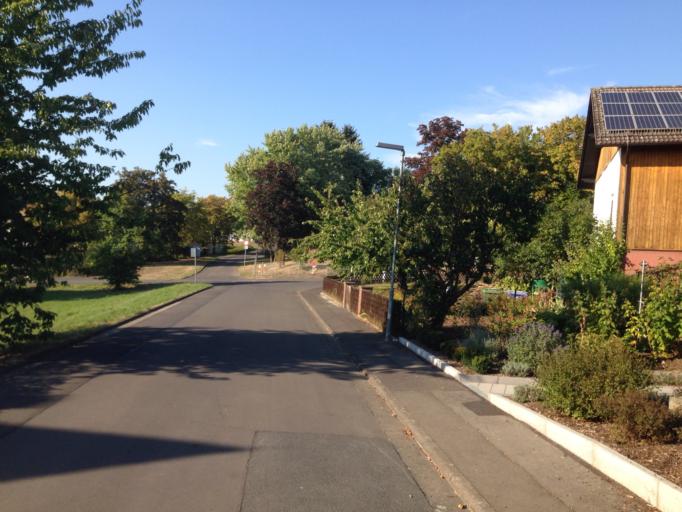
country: DE
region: Hesse
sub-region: Regierungsbezirk Giessen
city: Grossen Buseck
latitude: 50.5459
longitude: 8.7396
